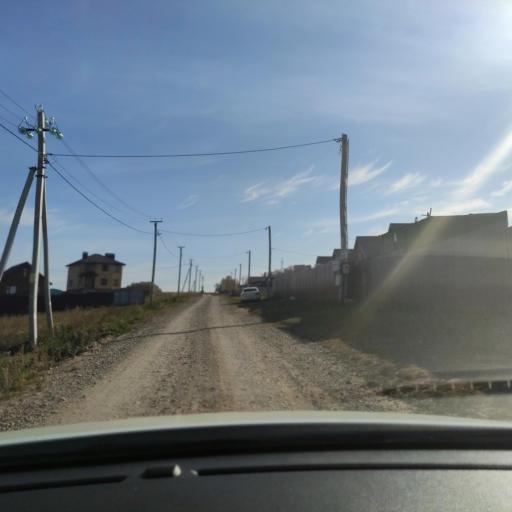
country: RU
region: Tatarstan
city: Vysokaya Gora
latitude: 55.7478
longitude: 49.4075
